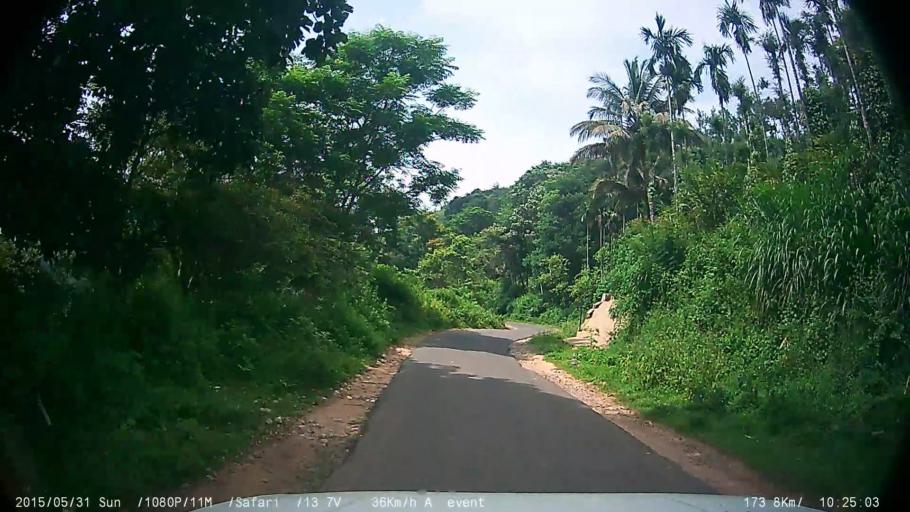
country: IN
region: Kerala
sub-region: Wayanad
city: Kalpetta
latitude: 11.5317
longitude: 76.1386
